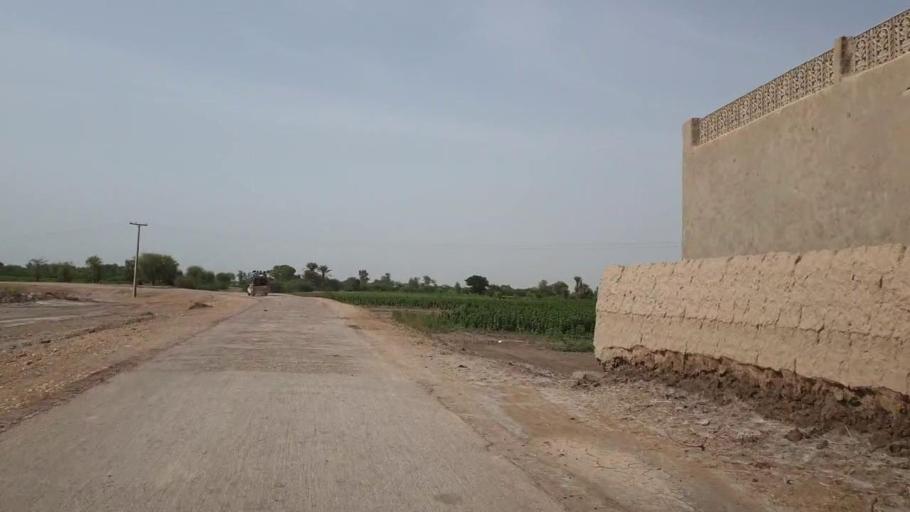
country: PK
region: Sindh
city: Bandhi
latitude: 26.5698
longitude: 68.3805
